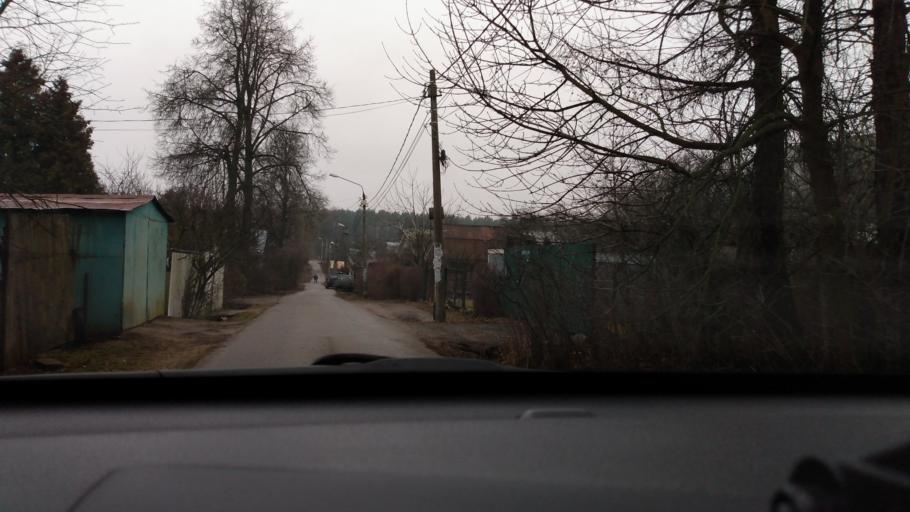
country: RU
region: Moskovskaya
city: Lesnoy Gorodok
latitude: 55.6628
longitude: 37.1756
